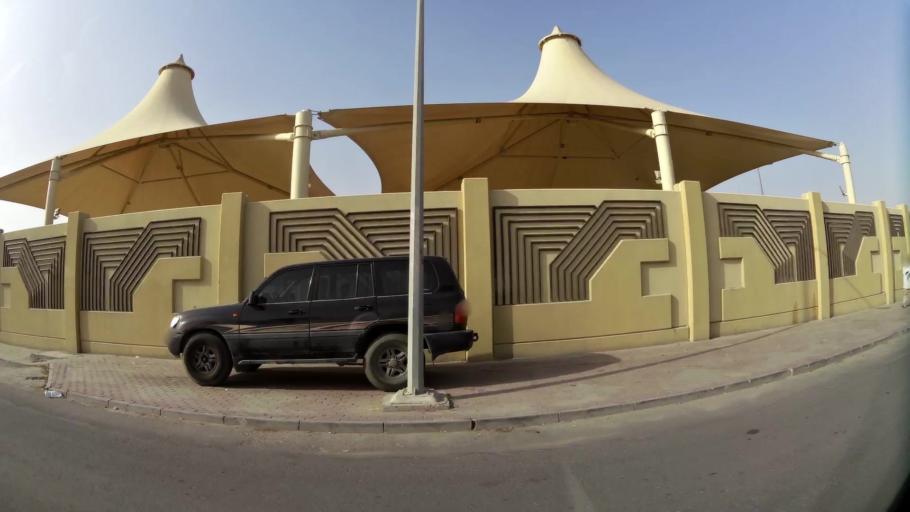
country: QA
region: Baladiyat ar Rayyan
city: Ar Rayyan
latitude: 25.2330
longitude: 51.4332
